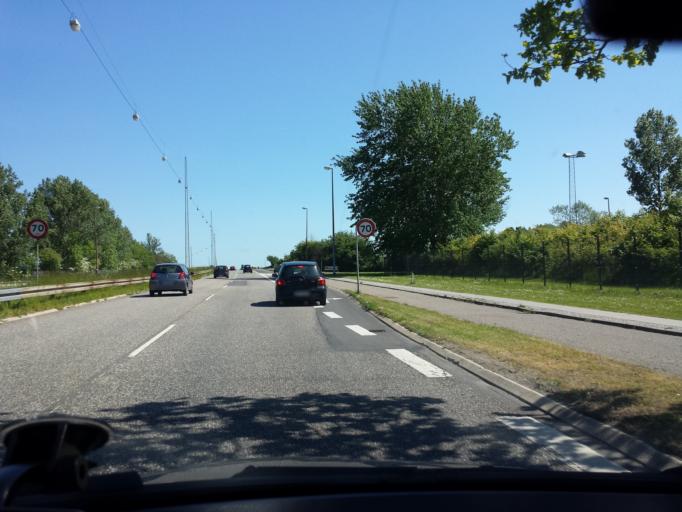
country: DK
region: Capital Region
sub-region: Herlev Kommune
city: Herlev
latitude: 55.7072
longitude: 12.4244
